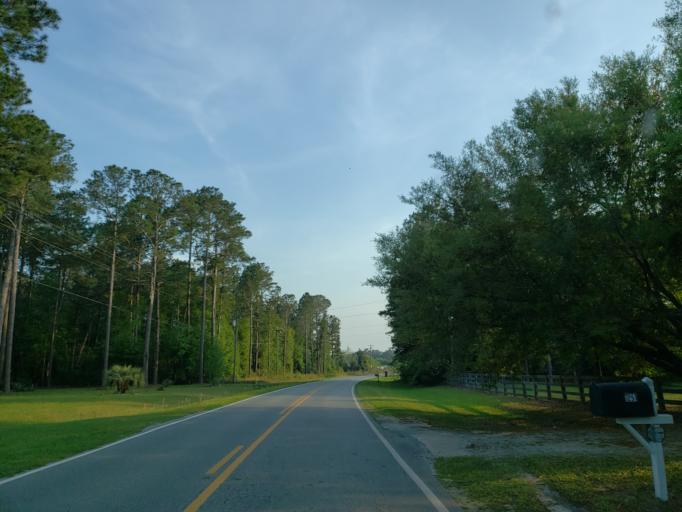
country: US
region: Georgia
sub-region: Cook County
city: Sparks
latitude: 31.1837
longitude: -83.4275
